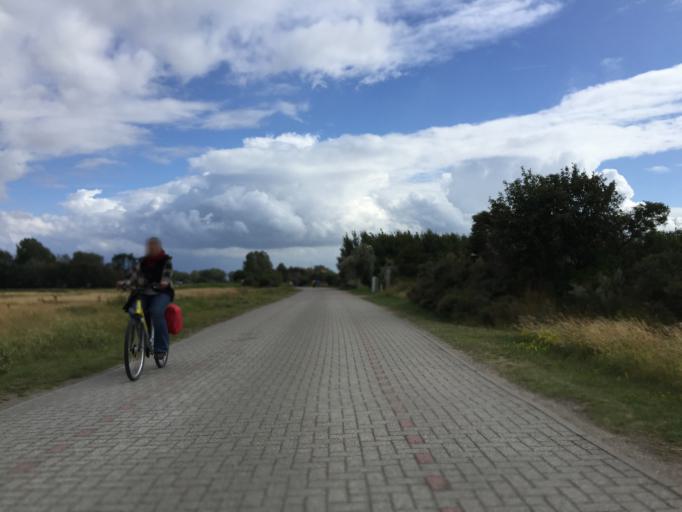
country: DE
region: Mecklenburg-Vorpommern
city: Hiddensee
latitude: 54.5761
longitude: 13.1044
